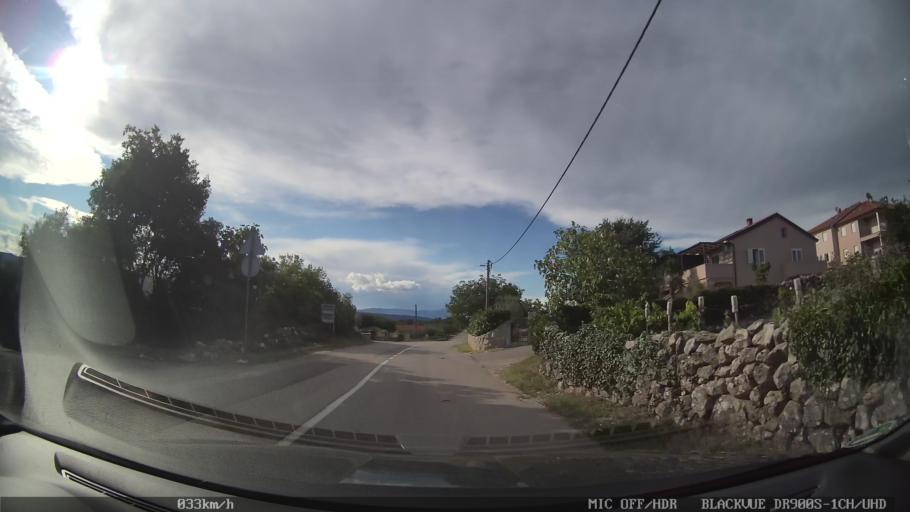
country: HR
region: Primorsko-Goranska
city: Njivice
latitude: 45.0746
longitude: 14.4638
